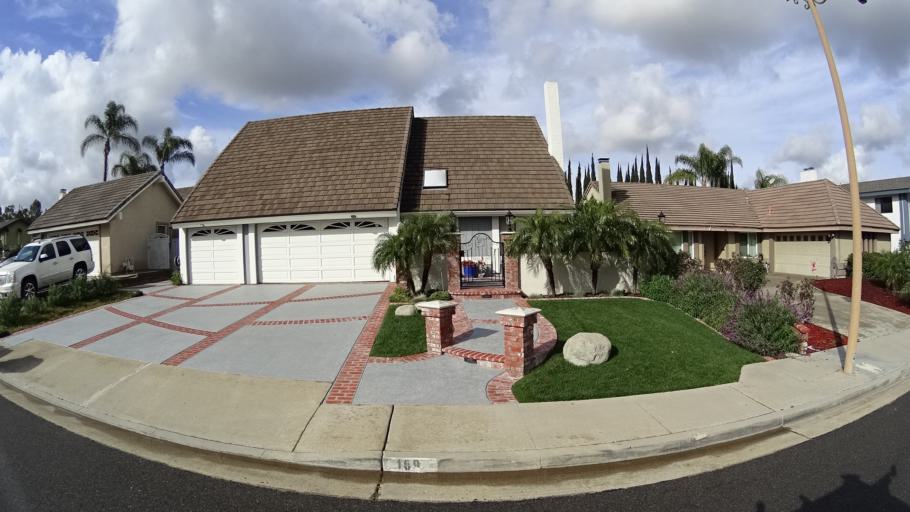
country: US
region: California
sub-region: Orange County
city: Villa Park
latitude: 33.8500
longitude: -117.7802
